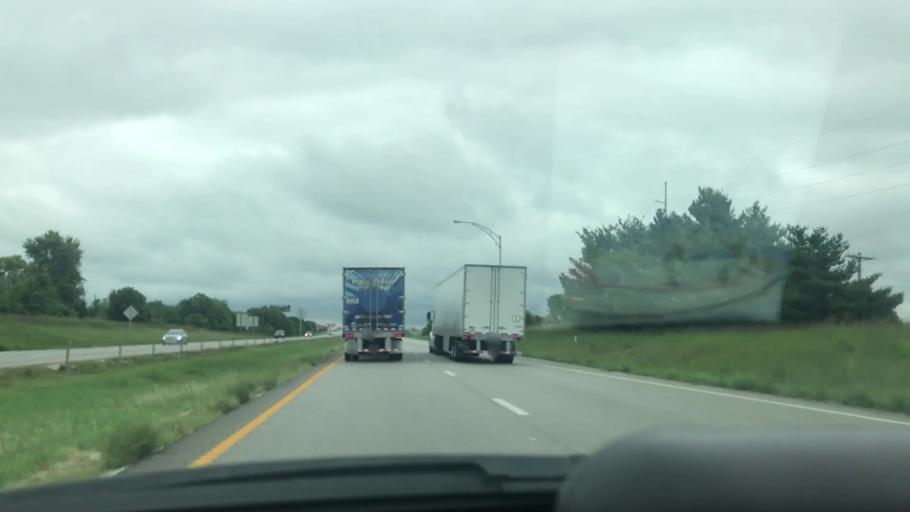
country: US
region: Missouri
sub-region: Greene County
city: Springfield
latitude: 37.2156
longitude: -93.3817
